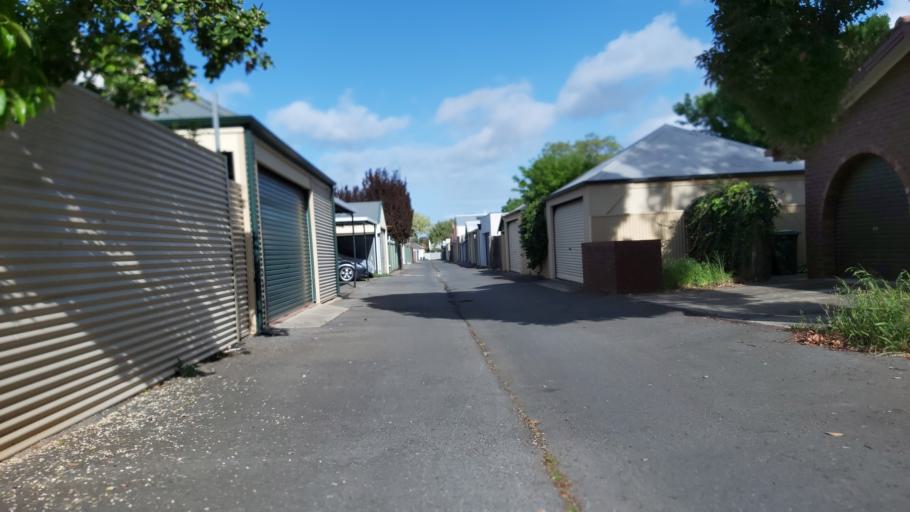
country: AU
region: South Australia
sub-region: Unley
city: Unley
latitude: -34.9433
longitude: 138.5954
